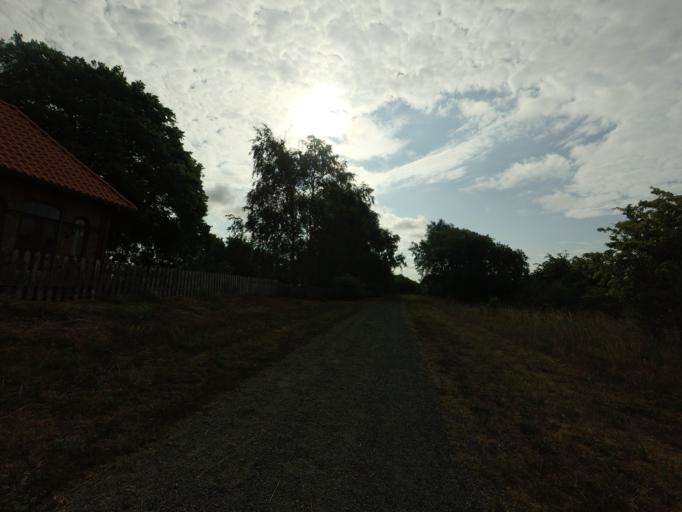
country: SE
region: Skane
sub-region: Helsingborg
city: Odakra
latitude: 56.1666
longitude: 12.7298
